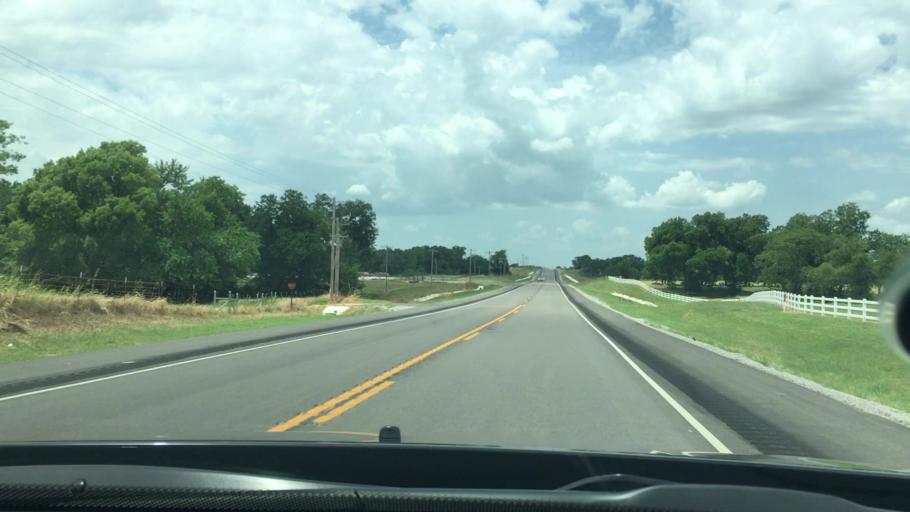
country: US
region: Oklahoma
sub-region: Love County
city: Marietta
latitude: 33.9404
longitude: -97.1967
